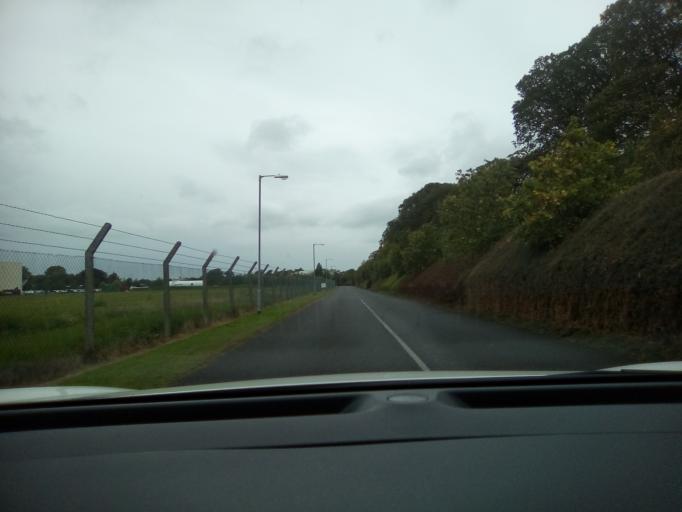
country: IE
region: Leinster
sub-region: Kildare
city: Leixlip
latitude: 53.3563
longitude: -6.4843
